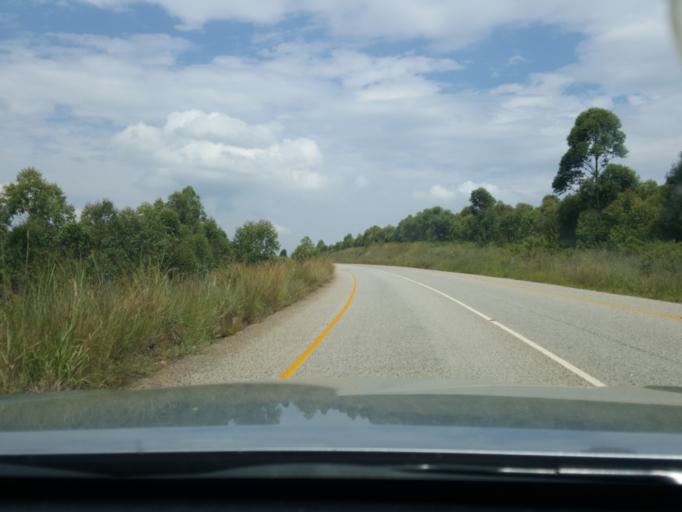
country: ZA
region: Mpumalanga
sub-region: Ehlanzeni District
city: White River
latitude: -25.1900
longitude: 30.9056
